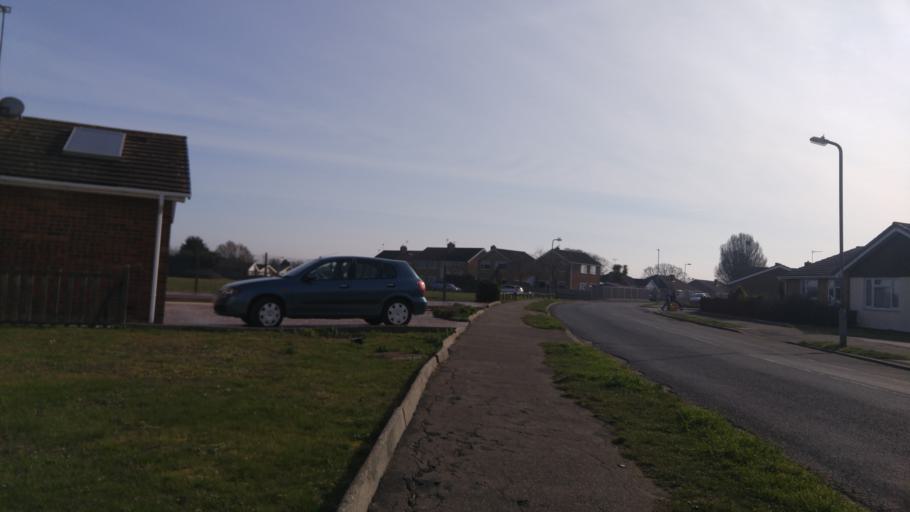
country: GB
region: England
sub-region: Essex
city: Little Clacton
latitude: 51.8143
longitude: 1.1653
